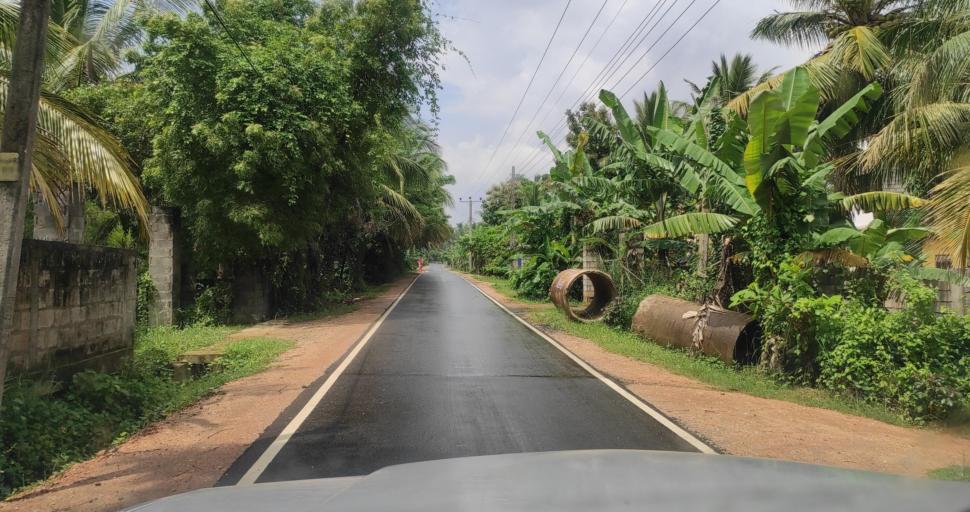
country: LK
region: Eastern Province
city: Trincomalee
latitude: 8.3737
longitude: 81.0101
